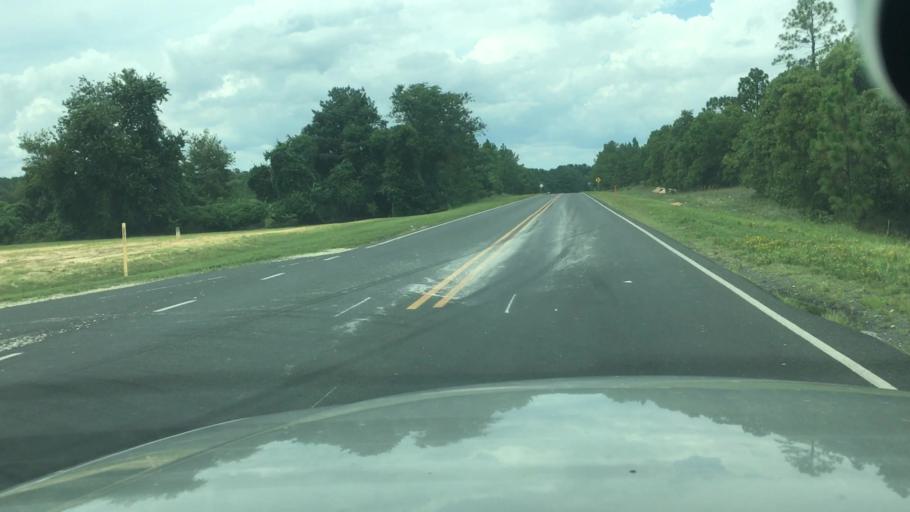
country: US
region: North Carolina
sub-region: Cumberland County
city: Hope Mills
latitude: 34.9716
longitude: -78.8933
